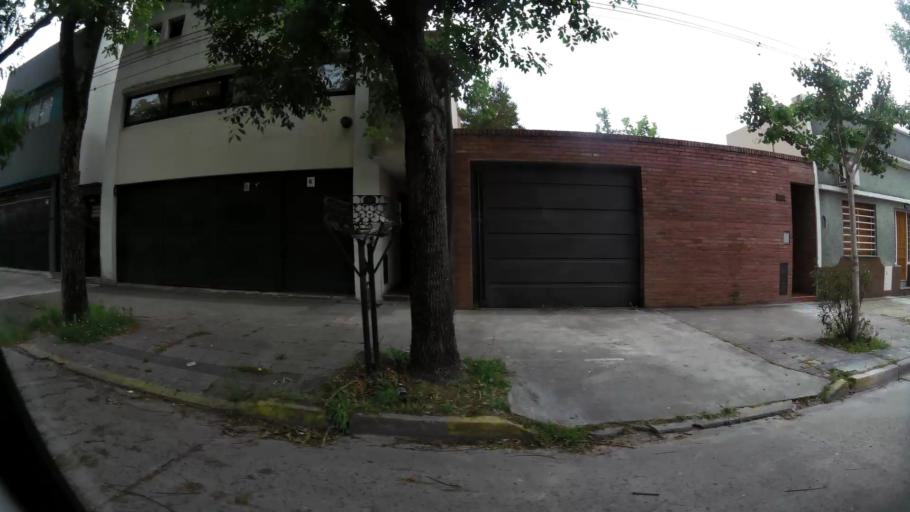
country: AR
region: Buenos Aires
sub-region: Partido de La Plata
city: La Plata
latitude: -34.9395
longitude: -57.9678
